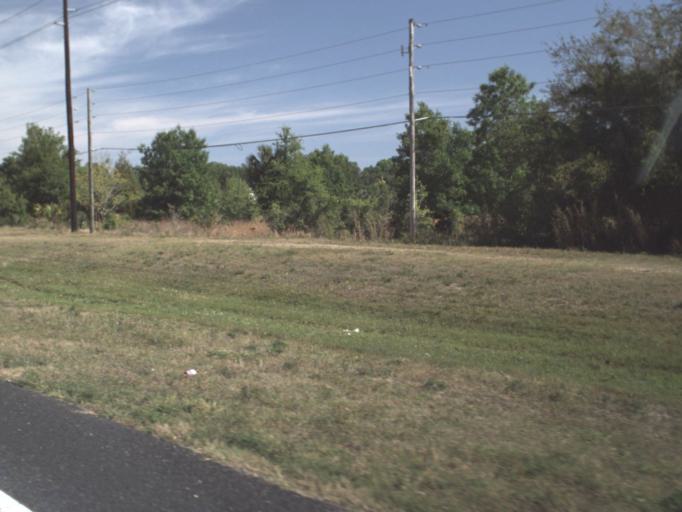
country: US
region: Florida
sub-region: Lake County
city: Hawthorne
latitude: 28.7667
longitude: -81.8823
